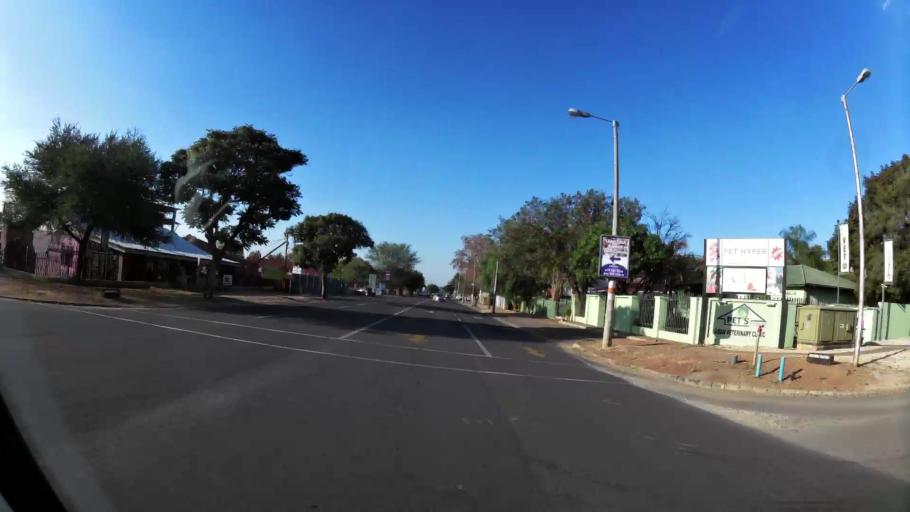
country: ZA
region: North-West
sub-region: Bojanala Platinum District Municipality
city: Rustenburg
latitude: -25.6788
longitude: 27.2351
